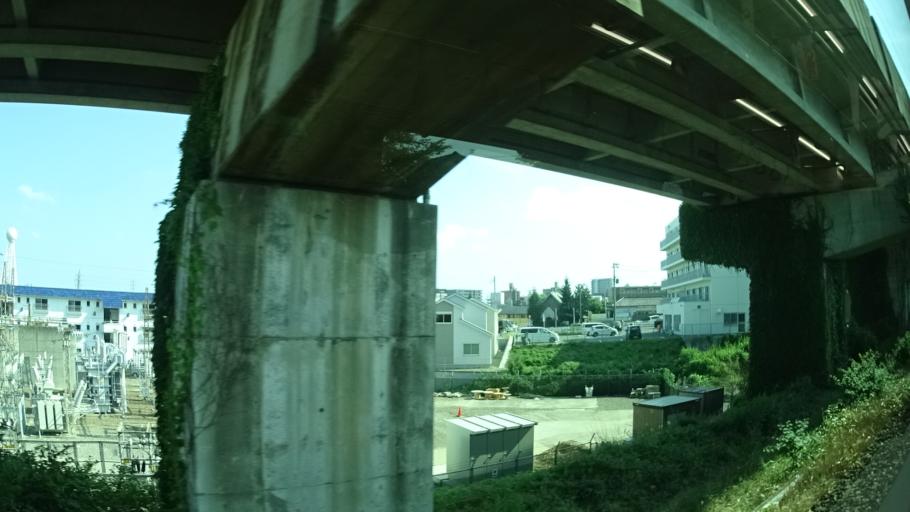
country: JP
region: Miyagi
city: Sendai-shi
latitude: 38.2713
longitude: 140.9112
